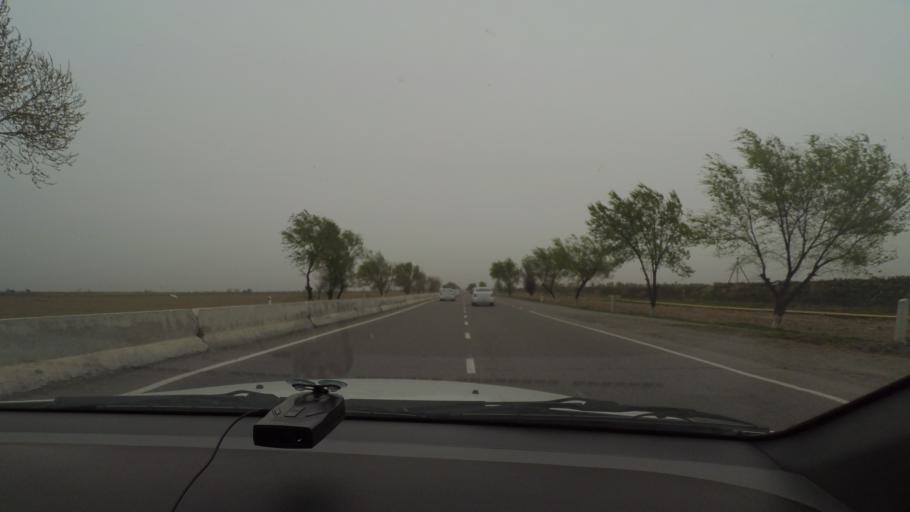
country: UZ
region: Jizzax
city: Gagarin
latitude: 40.5279
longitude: 68.3390
